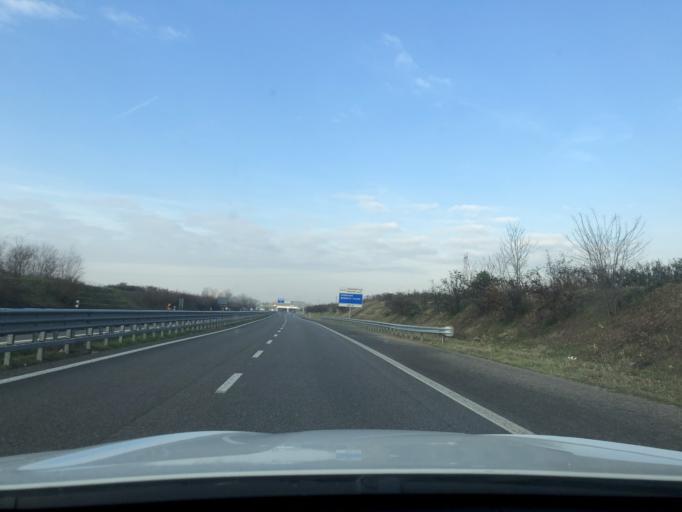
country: IT
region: Lombardy
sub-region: Citta metropolitana di Milano
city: Casate
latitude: 45.4967
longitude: 8.8395
